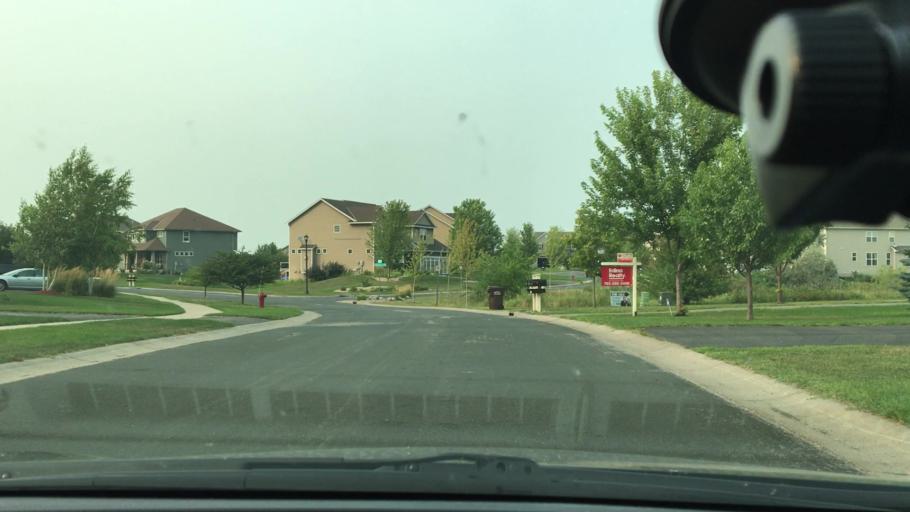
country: US
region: Minnesota
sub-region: Wright County
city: Albertville
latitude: 45.2499
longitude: -93.6447
